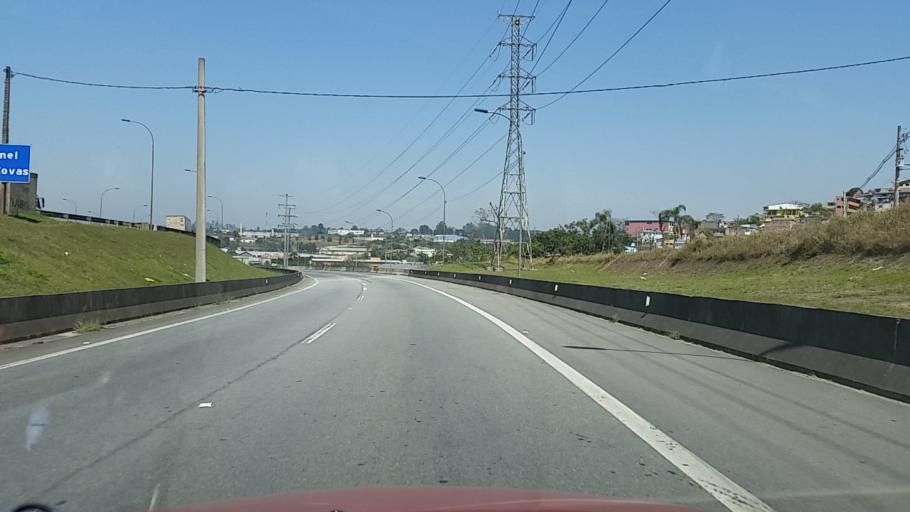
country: BR
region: Sao Paulo
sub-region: Embu
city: Embu
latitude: -23.6357
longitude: -46.8344
